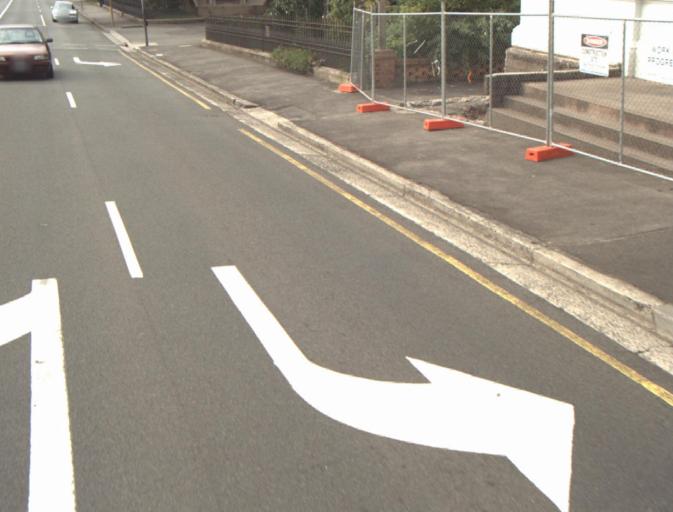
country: AU
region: Tasmania
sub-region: Launceston
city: Launceston
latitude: -41.4341
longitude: 147.1422
